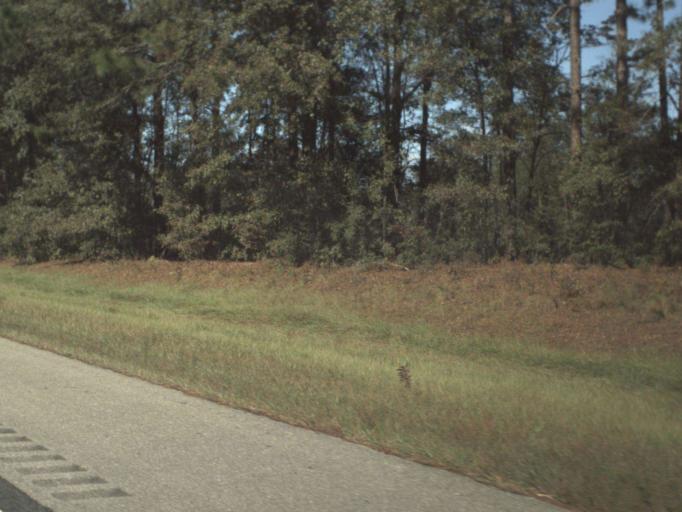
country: US
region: Florida
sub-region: Washington County
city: Chipley
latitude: 30.7462
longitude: -85.4955
